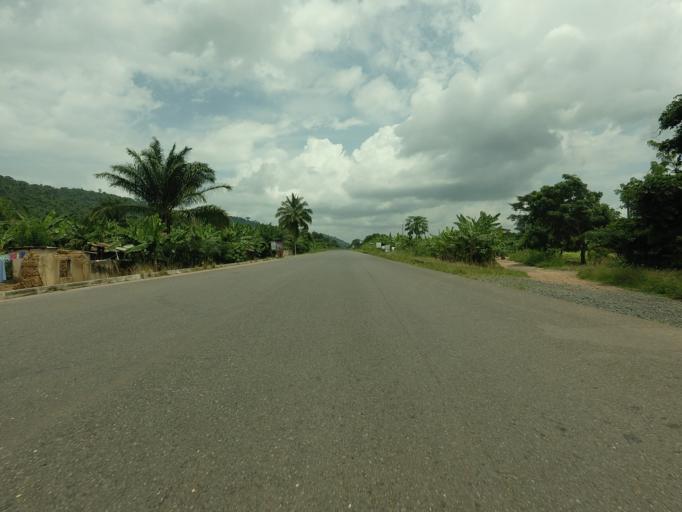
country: GH
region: Volta
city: Ho
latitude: 6.4980
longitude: 0.2040
